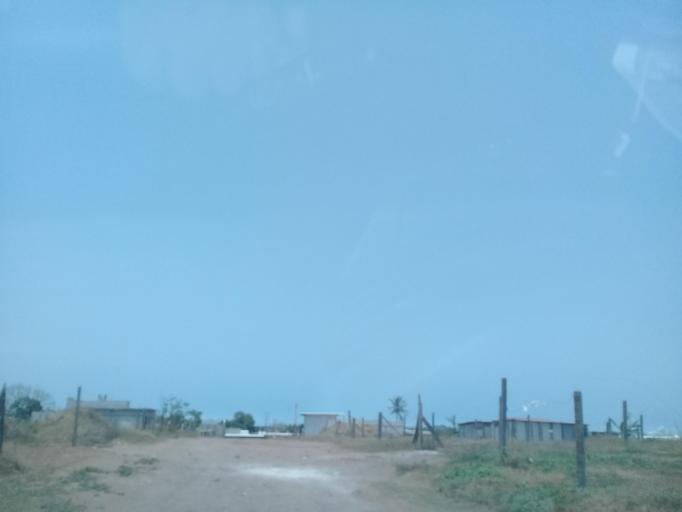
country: MX
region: Veracruz
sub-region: Veracruz
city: Las Amapolas
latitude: 19.1578
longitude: -96.2151
